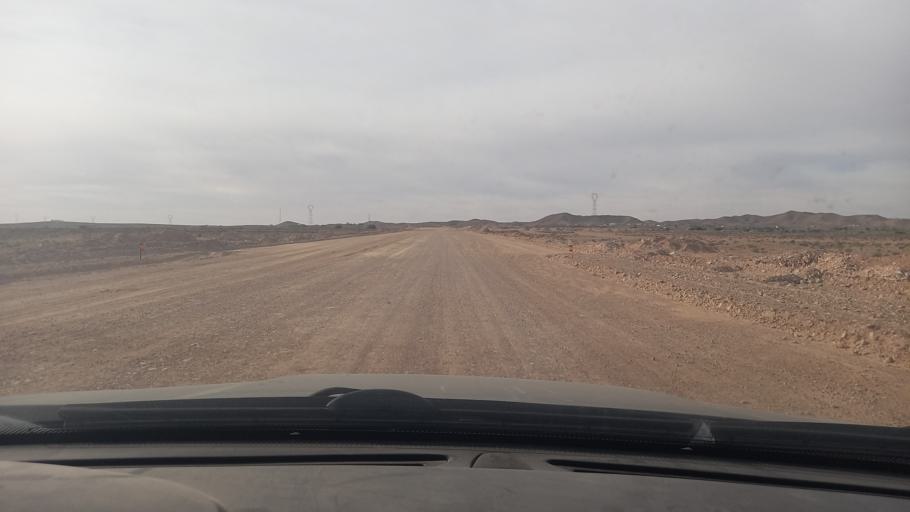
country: TN
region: Tataouine
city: Tataouine
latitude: 33.1339
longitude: 10.5036
